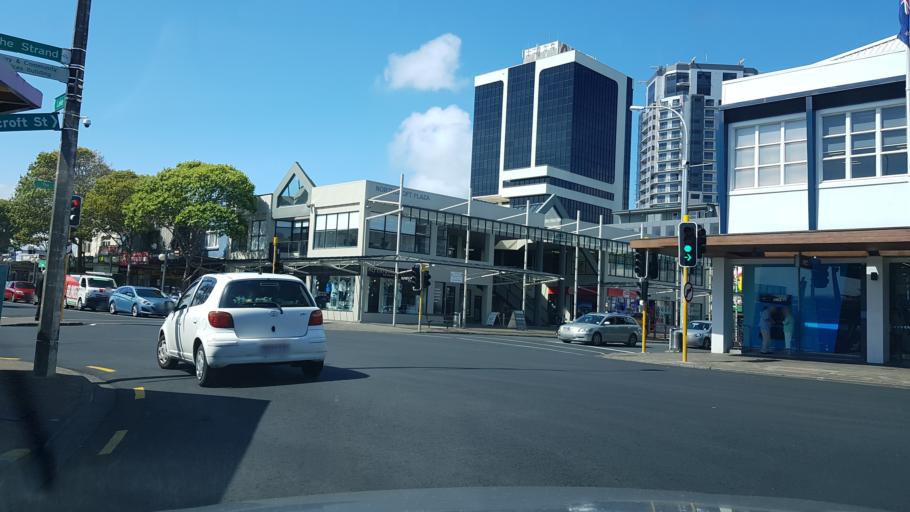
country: NZ
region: Auckland
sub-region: Auckland
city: North Shore
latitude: -36.7890
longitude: 174.7724
